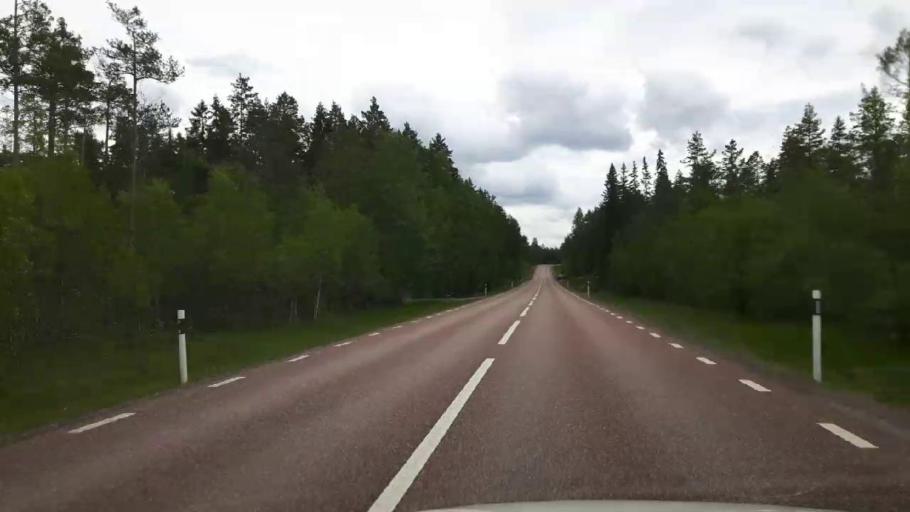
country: SE
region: Dalarna
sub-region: Hedemora Kommun
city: Brunna
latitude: 60.1947
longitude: 15.9976
